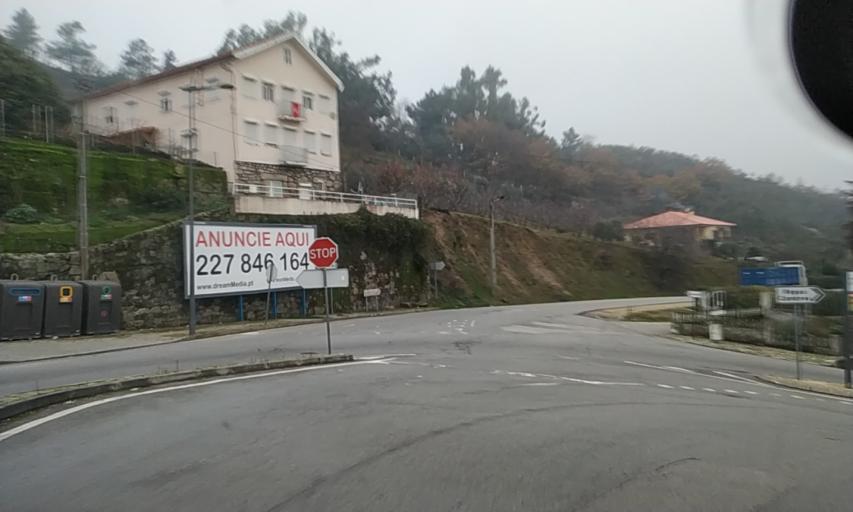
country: PT
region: Viseu
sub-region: Lamego
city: Lamego
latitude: 41.1119
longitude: -7.8065
